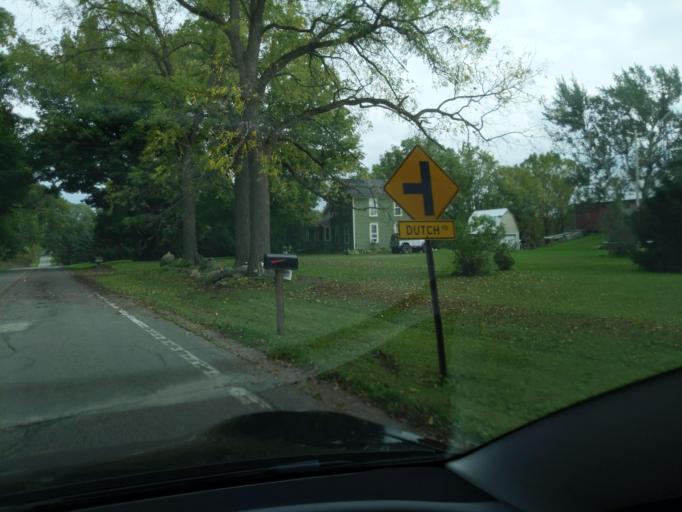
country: US
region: Michigan
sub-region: Ingham County
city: Leslie
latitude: 42.4113
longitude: -84.4019
